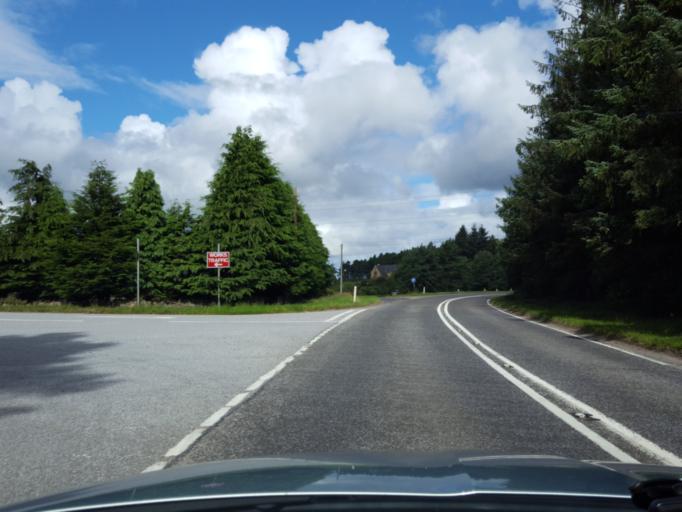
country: GB
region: Scotland
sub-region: Moray
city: Lhanbryd
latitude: 57.5818
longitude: -3.2790
